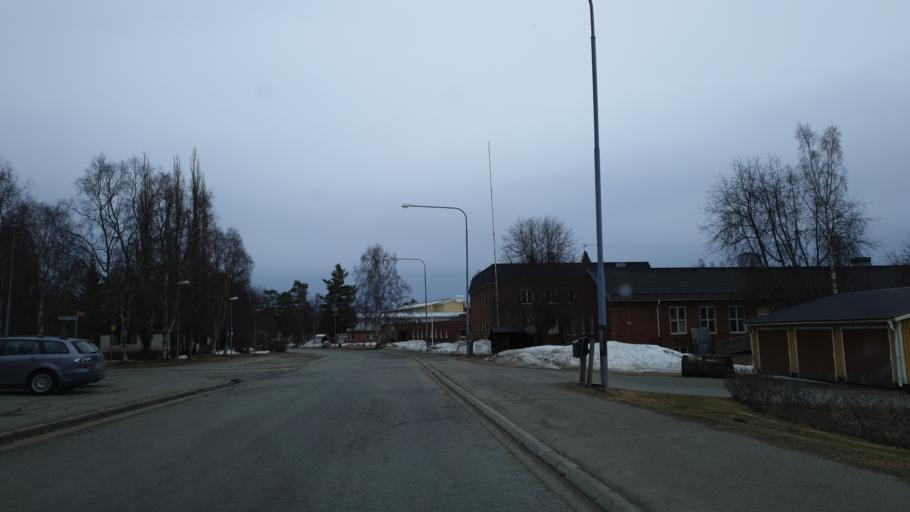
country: SE
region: Vaesterbotten
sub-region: Skelleftea Kommun
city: Byske
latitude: 64.9523
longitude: 21.2030
